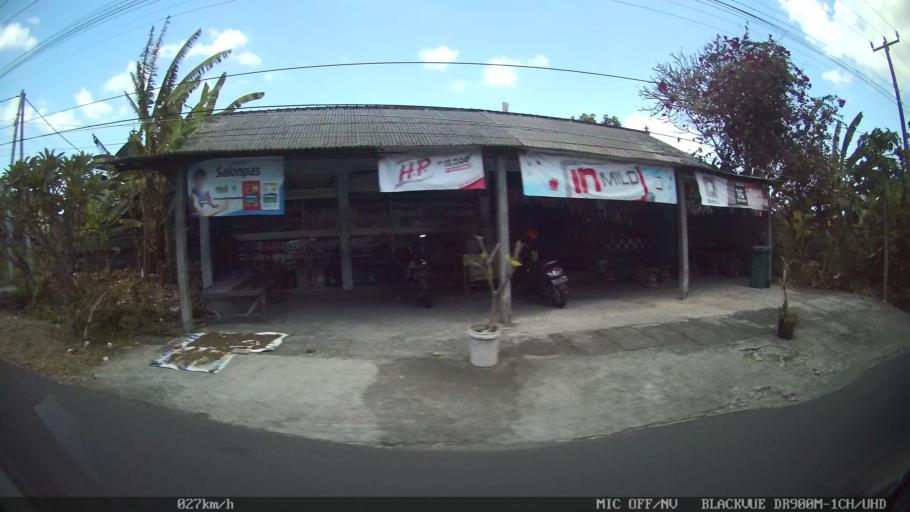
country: ID
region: Bali
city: Banjar Gunungpande
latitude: -8.6514
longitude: 115.1584
